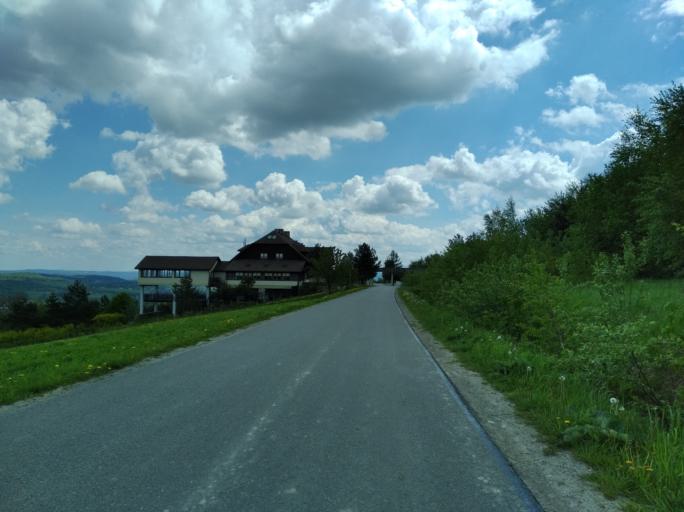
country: PL
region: Subcarpathian Voivodeship
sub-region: Powiat jasielski
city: Kolaczyce
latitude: 49.8369
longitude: 21.5193
